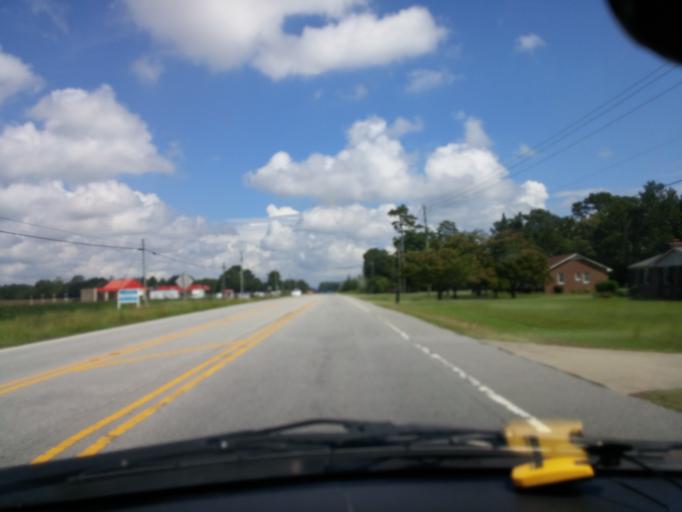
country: US
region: North Carolina
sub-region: Duplin County
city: Beulaville
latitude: 35.0709
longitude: -77.7363
